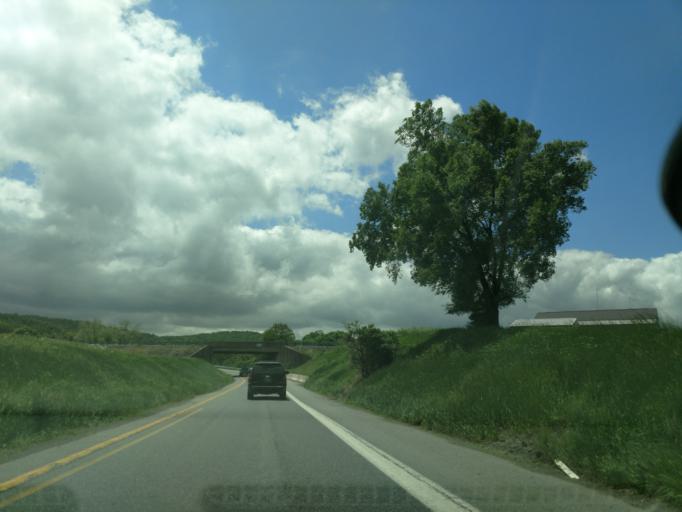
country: US
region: Pennsylvania
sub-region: Lebanon County
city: Cornwall
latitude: 40.2723
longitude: -76.4377
